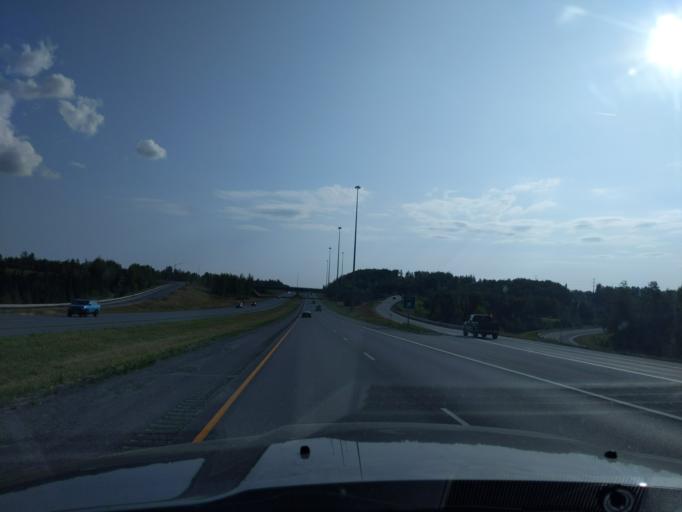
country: US
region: Alaska
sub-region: Anchorage Municipality
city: Eagle River
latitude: 61.3452
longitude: -149.5596
